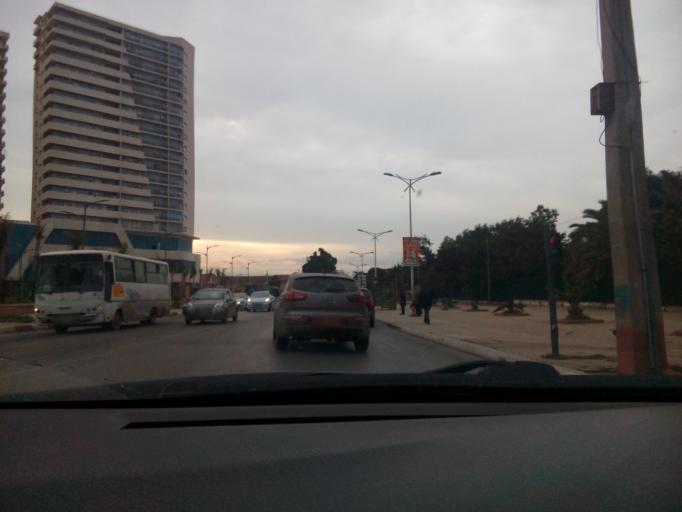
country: DZ
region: Oran
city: Oran
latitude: 35.6817
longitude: -0.6367
